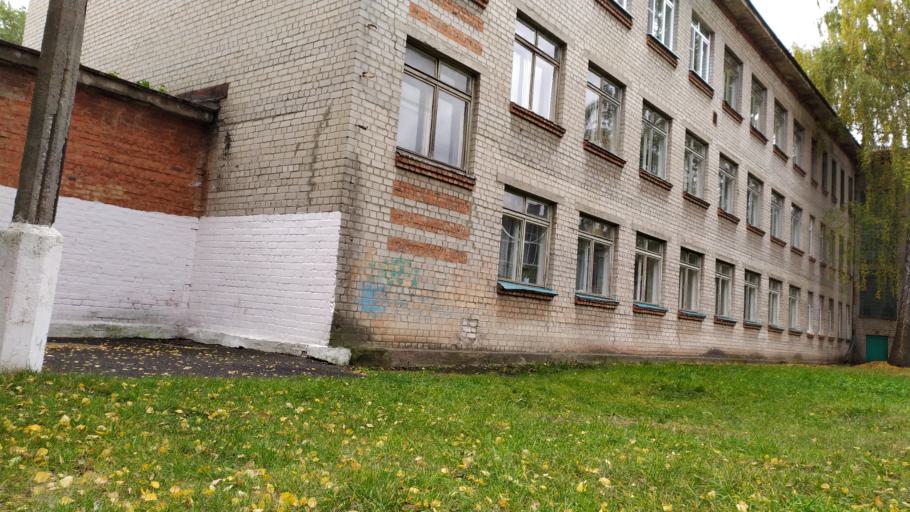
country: RU
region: Kursk
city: Kursk
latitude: 51.6499
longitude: 36.1422
